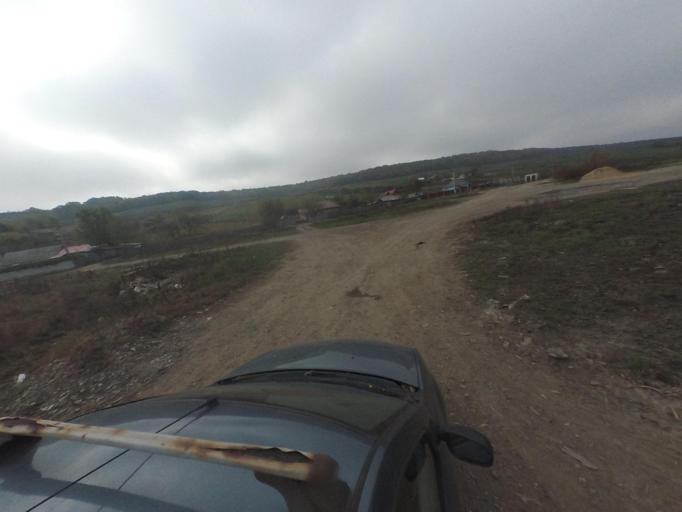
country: RO
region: Vaslui
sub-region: Comuna Bacesti
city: Bacesti
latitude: 46.8368
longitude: 27.2285
